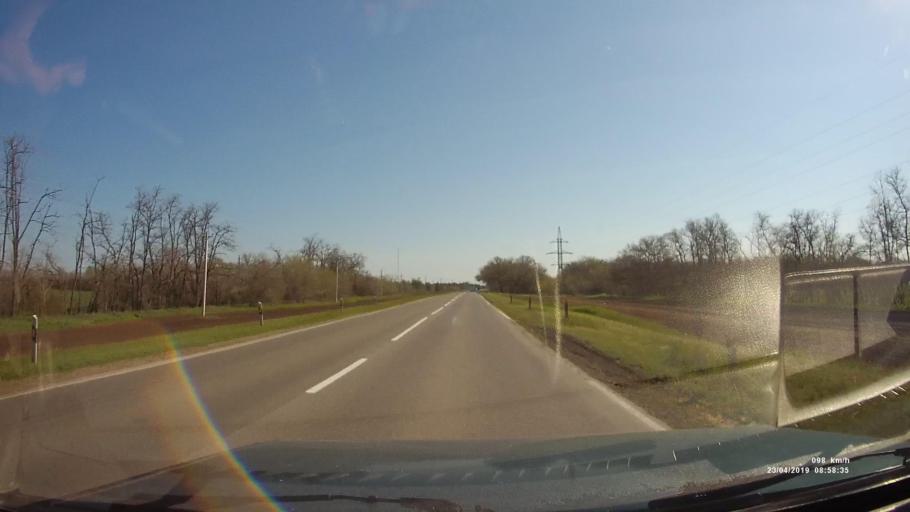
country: RU
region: Rostov
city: Sal'sk
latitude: 46.5112
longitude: 41.5423
